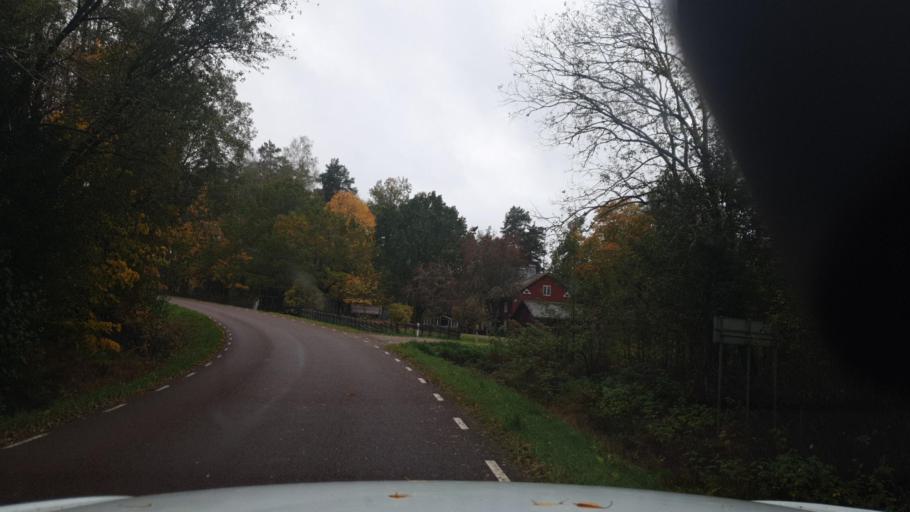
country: SE
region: Vaermland
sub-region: Karlstads Kommun
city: Valberg
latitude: 59.4316
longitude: 13.0848
